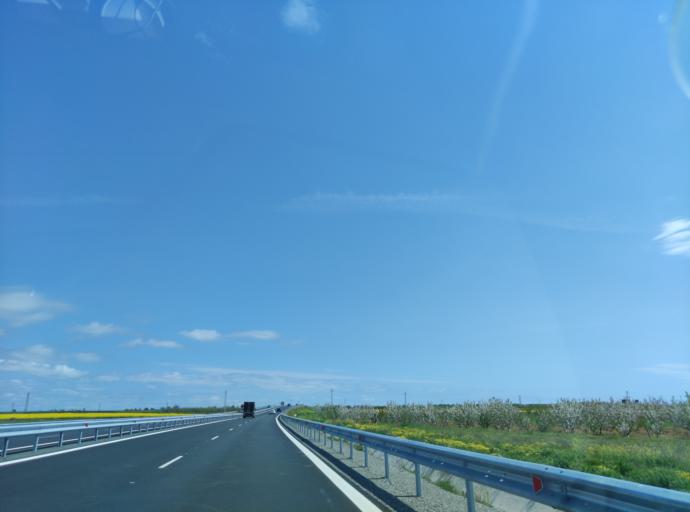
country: BG
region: Burgas
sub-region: Obshtina Pomorie
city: Pomorie
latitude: 42.5758
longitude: 27.5769
